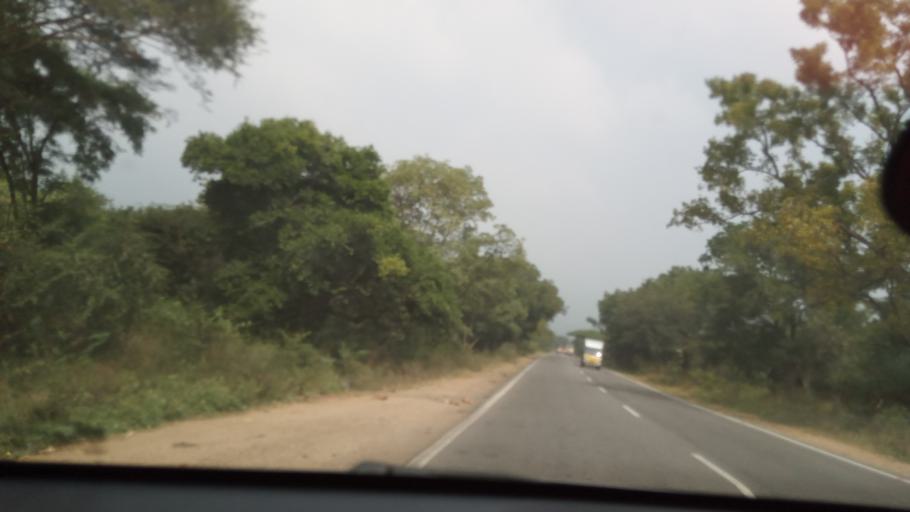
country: IN
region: Tamil Nadu
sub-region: Erode
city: Sathyamangalam
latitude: 11.5610
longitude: 77.1360
